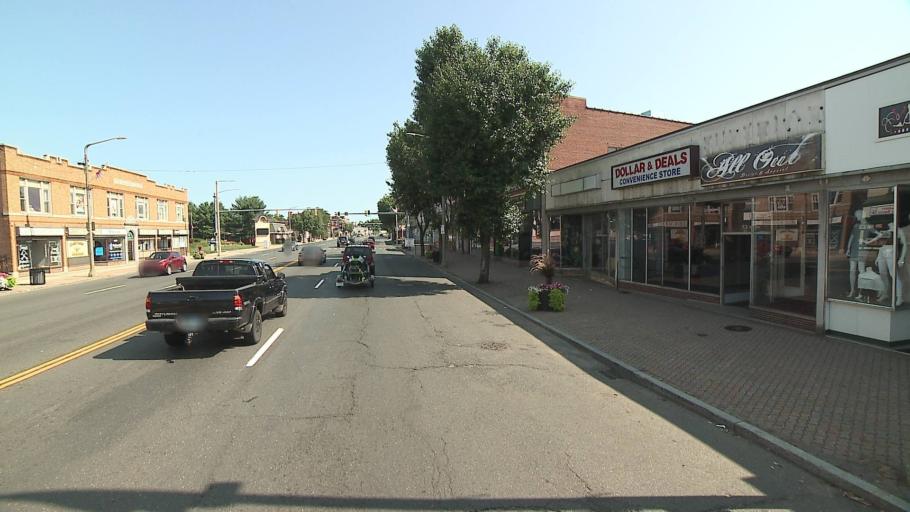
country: US
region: Connecticut
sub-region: Hartford County
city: East Hartford
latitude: 41.7710
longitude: -72.6427
